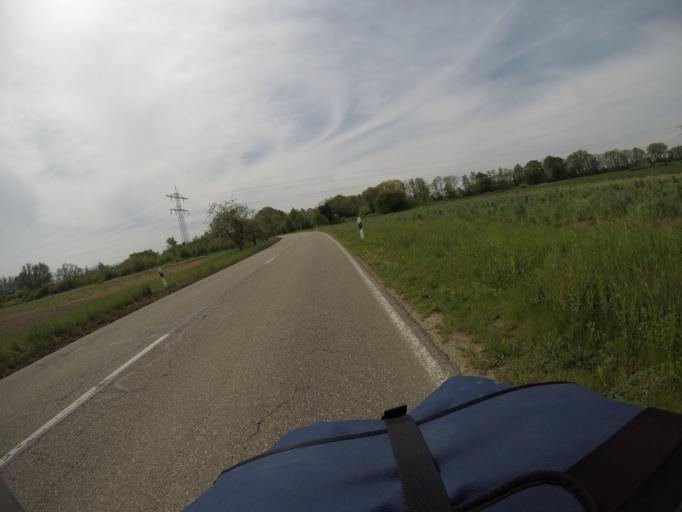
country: DE
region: Baden-Wuerttemberg
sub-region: Karlsruhe Region
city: Schwarzach
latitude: 48.7539
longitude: 8.0385
